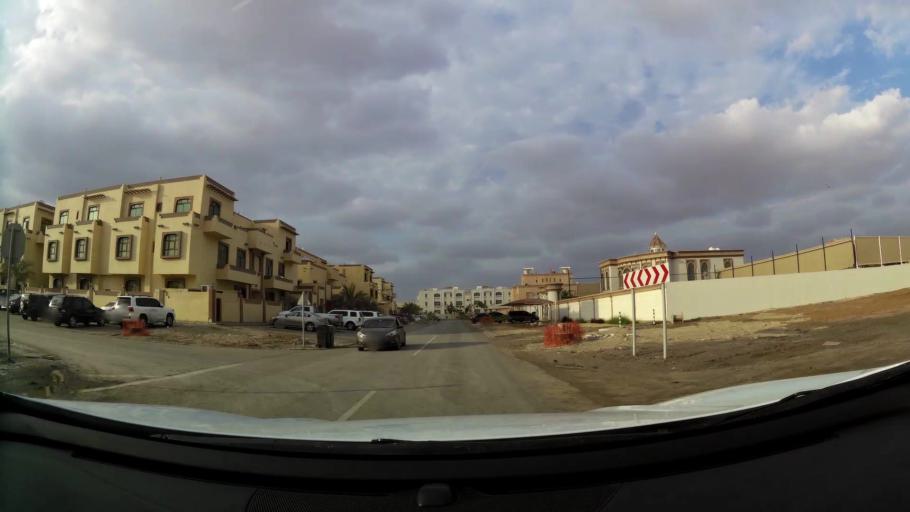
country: AE
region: Abu Dhabi
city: Abu Dhabi
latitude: 24.3553
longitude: 54.5515
